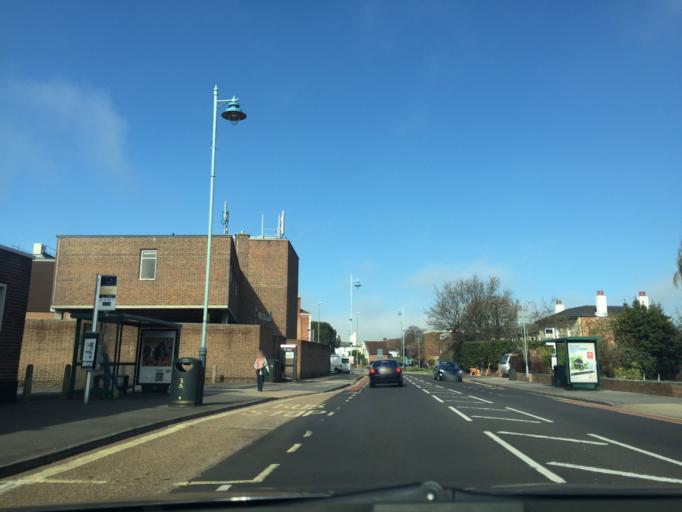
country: GB
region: England
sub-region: Hampshire
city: Gosport
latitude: 50.7923
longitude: -1.1387
